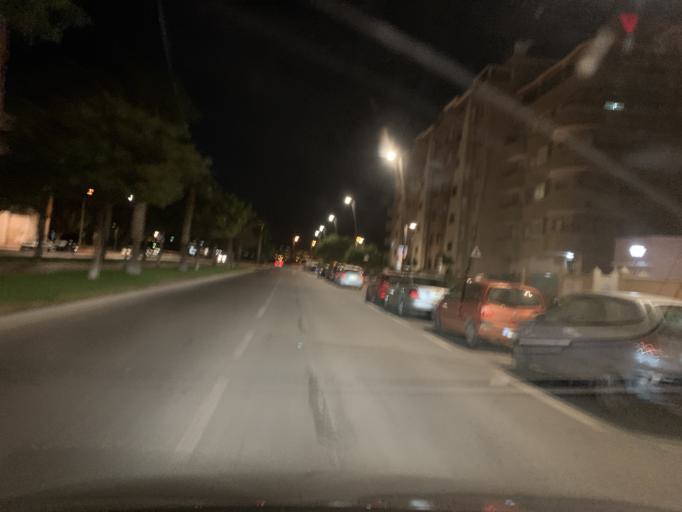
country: ES
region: Andalusia
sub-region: Provincia de Almeria
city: Roquetas de Mar
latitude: 36.7771
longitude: -2.6079
